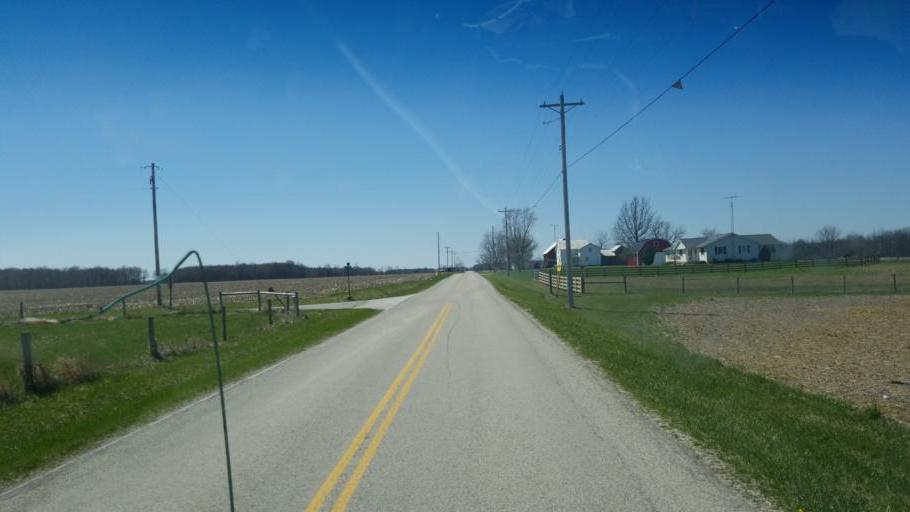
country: US
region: Ohio
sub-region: Huron County
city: Willard
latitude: 41.0544
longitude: -82.9193
